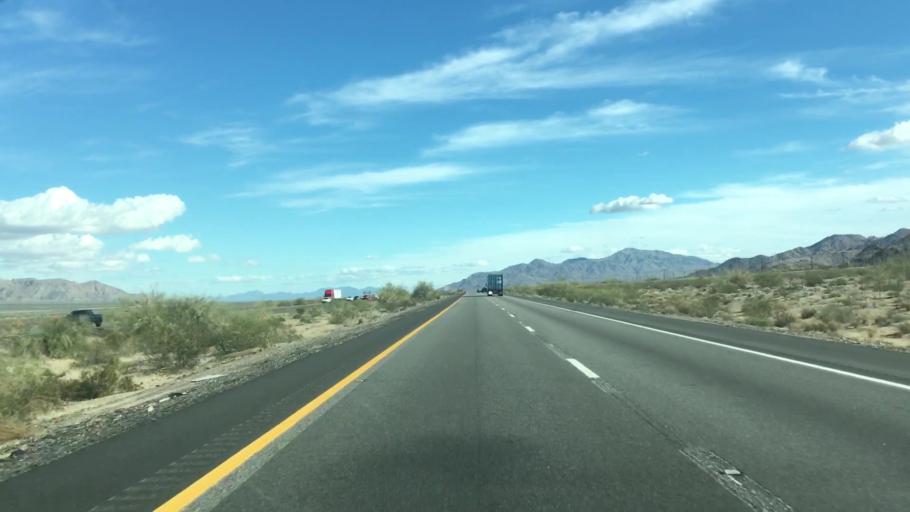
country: US
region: California
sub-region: Riverside County
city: Mecca
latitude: 33.6691
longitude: -115.6444
